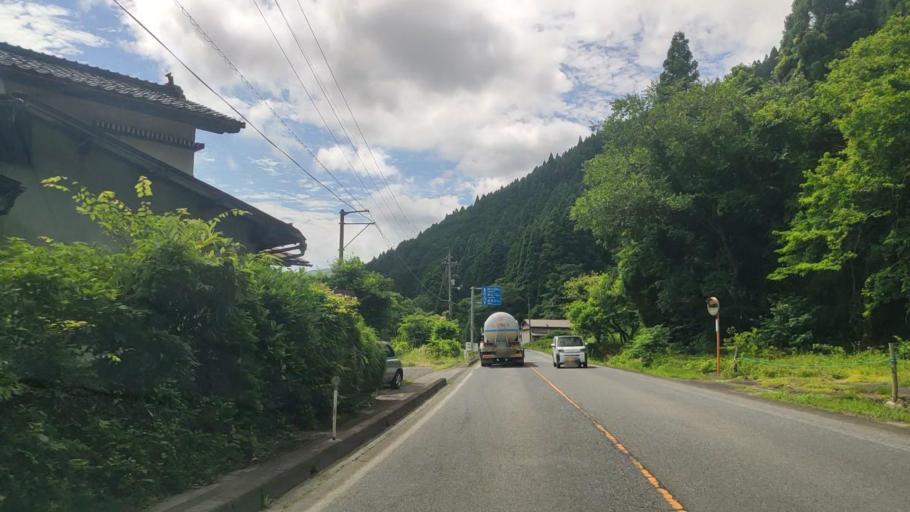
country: JP
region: Tottori
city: Yonago
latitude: 35.2331
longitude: 133.4393
